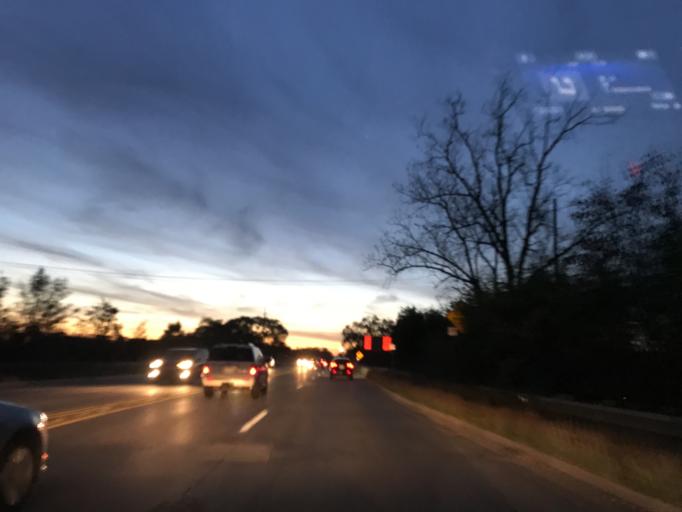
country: US
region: Michigan
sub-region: Wayne County
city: Northville
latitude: 42.4400
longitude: -83.4725
